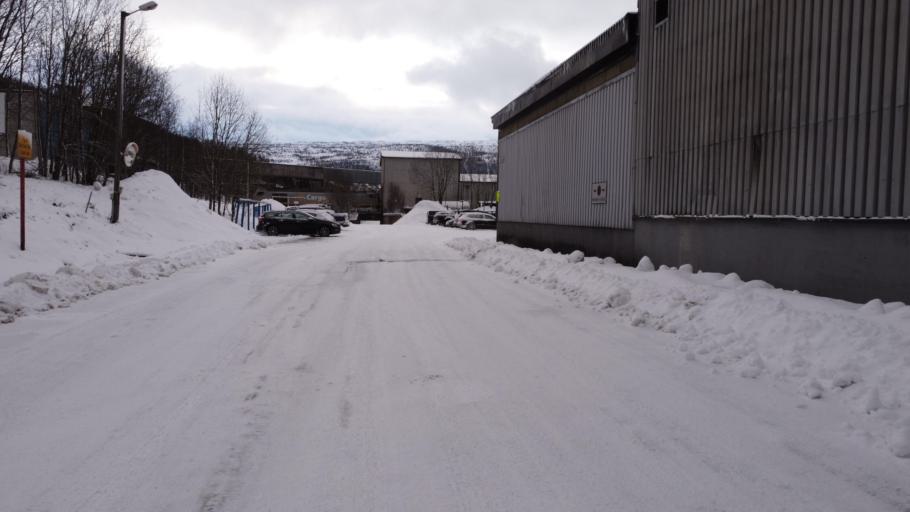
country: NO
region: Nordland
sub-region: Rana
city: Mo i Rana
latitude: 66.3269
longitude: 14.1519
